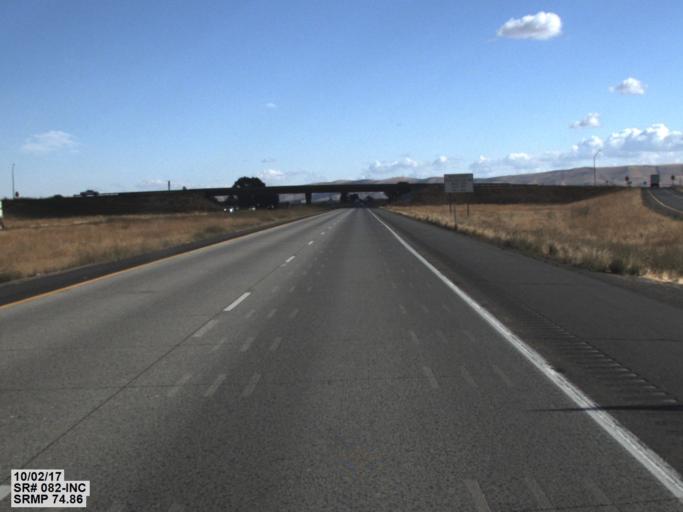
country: US
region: Washington
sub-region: Yakima County
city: Grandview
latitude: 46.2573
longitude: -119.8819
